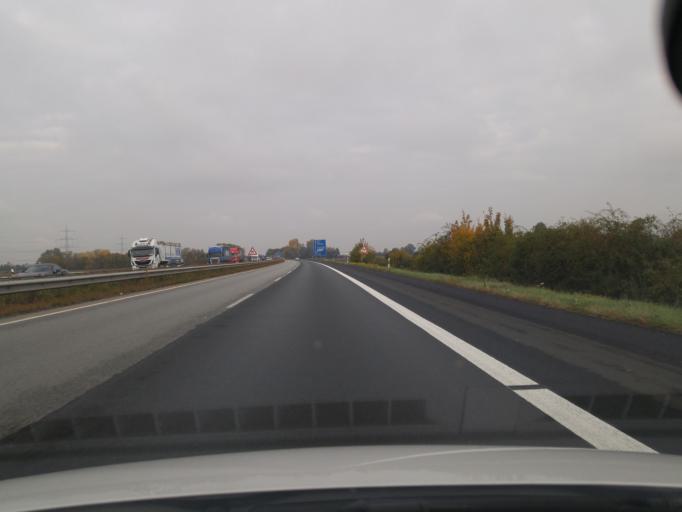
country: DE
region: Rheinland-Pfalz
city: Mutterstadt
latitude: 49.4222
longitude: 8.3380
